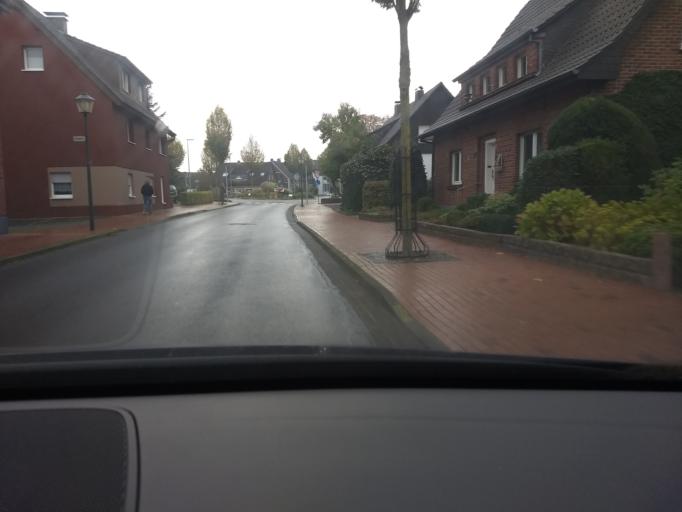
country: DE
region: North Rhine-Westphalia
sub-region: Regierungsbezirk Munster
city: Raesfeld
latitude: 51.7711
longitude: 6.8390
